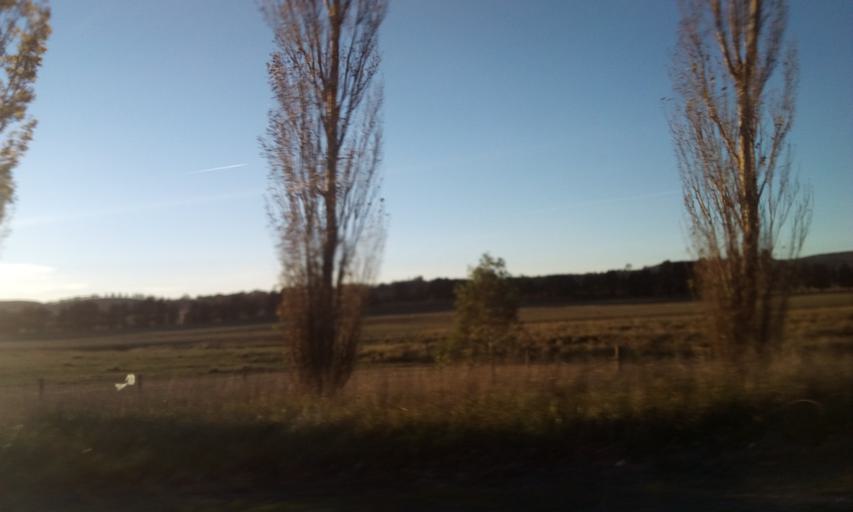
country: AU
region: New South Wales
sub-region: Goulburn Mulwaree
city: Goulburn
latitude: -34.8013
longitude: 149.6122
